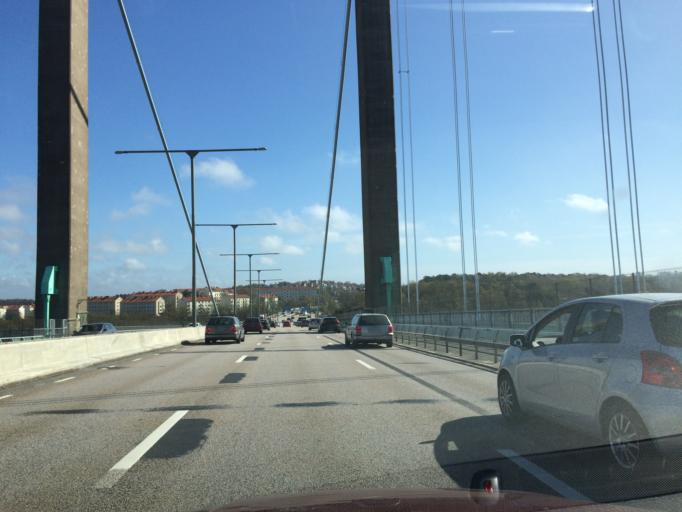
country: SE
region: Vaestra Goetaland
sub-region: Goteborg
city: Majorna
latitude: 57.6896
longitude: 11.9024
